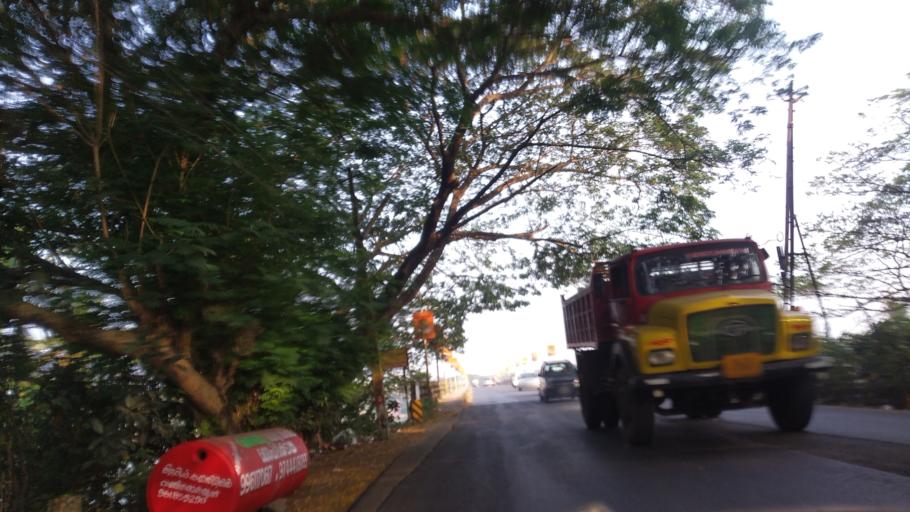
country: IN
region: Kerala
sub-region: Thrissur District
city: Kodungallur
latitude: 10.1921
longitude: 76.2014
